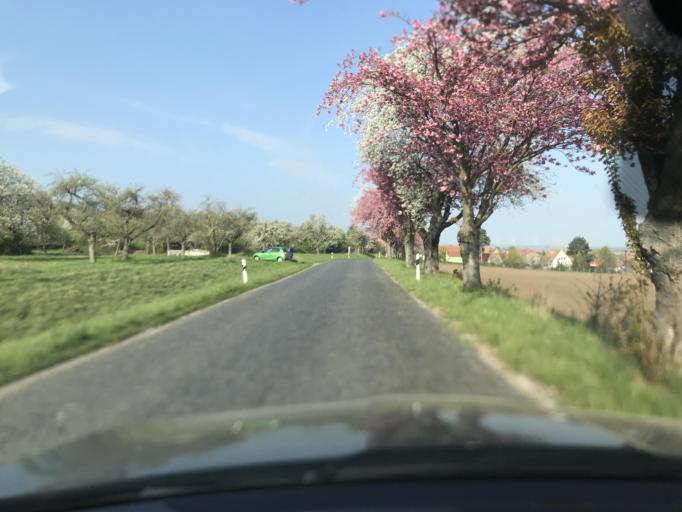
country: DE
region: Saxony-Anhalt
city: Strobeck
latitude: 51.9739
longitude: 10.9897
